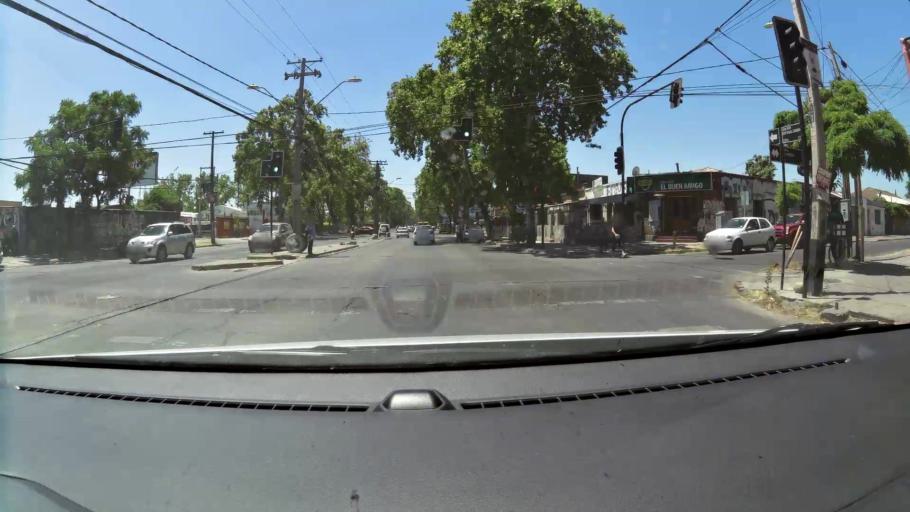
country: CL
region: Santiago Metropolitan
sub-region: Provincia de Maipo
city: San Bernardo
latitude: -33.5742
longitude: -70.6905
